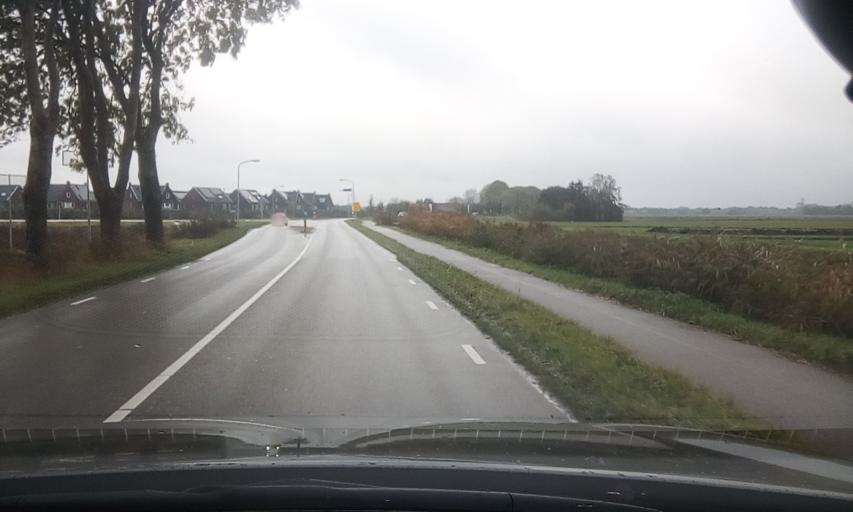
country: NL
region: Groningen
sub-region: Gemeente Groningen
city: Oosterpark
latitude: 53.2283
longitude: 6.6416
